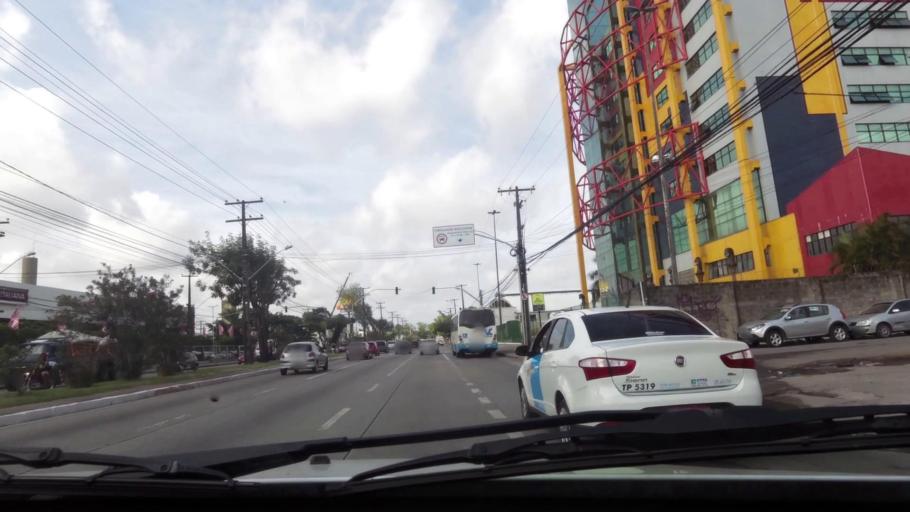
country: BR
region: Pernambuco
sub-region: Recife
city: Recife
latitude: -8.1006
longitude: -34.9102
